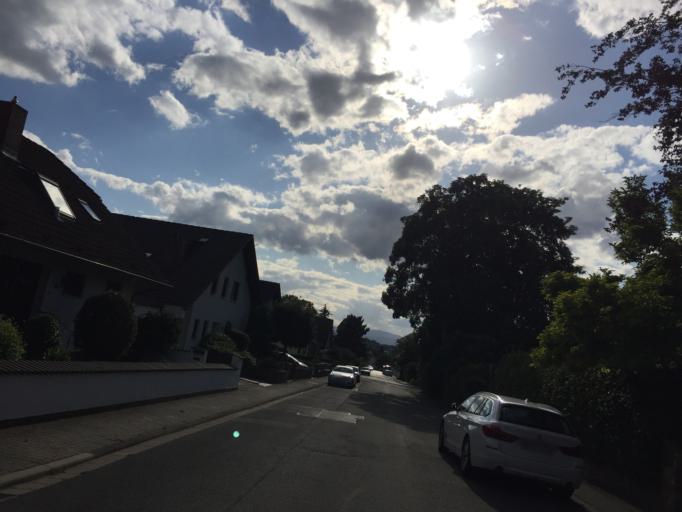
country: DE
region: Hesse
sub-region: Regierungsbezirk Darmstadt
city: Karben
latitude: 50.2301
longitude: 8.7774
